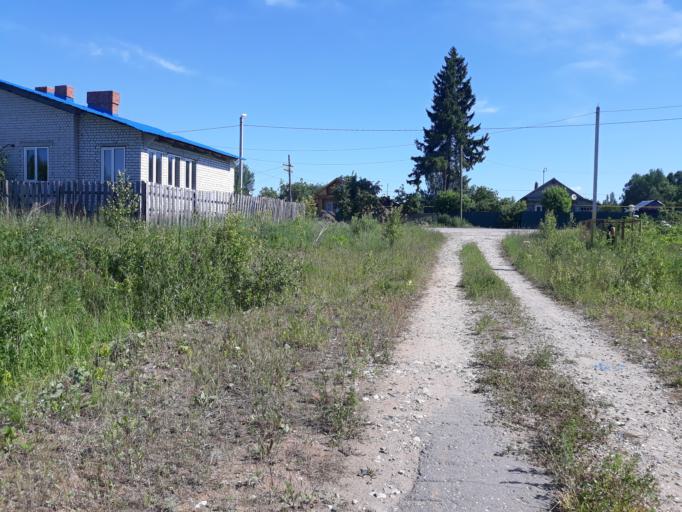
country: RU
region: Ivanovo
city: Novo-Talitsy
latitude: 57.0663
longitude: 40.7004
